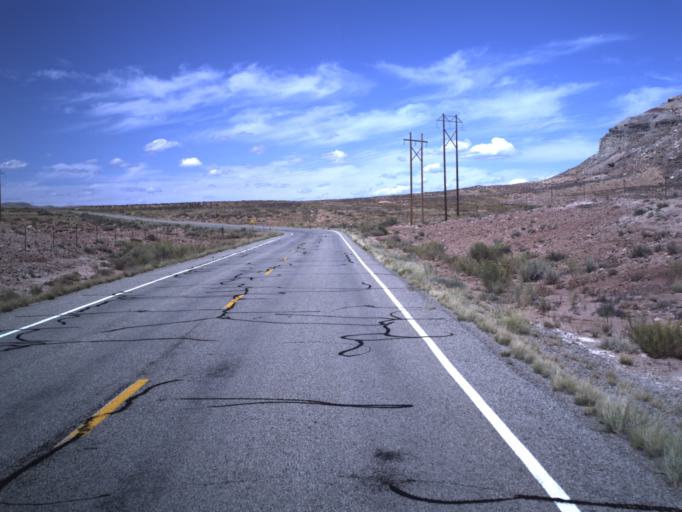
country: US
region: Utah
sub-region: San Juan County
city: Blanding
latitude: 37.2971
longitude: -109.4276
